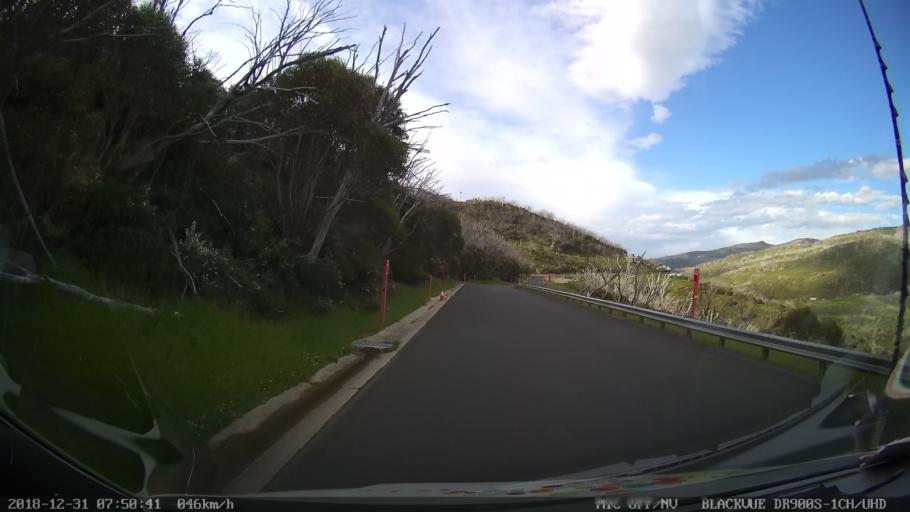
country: AU
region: New South Wales
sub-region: Snowy River
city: Jindabyne
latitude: -36.3751
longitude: 148.3793
